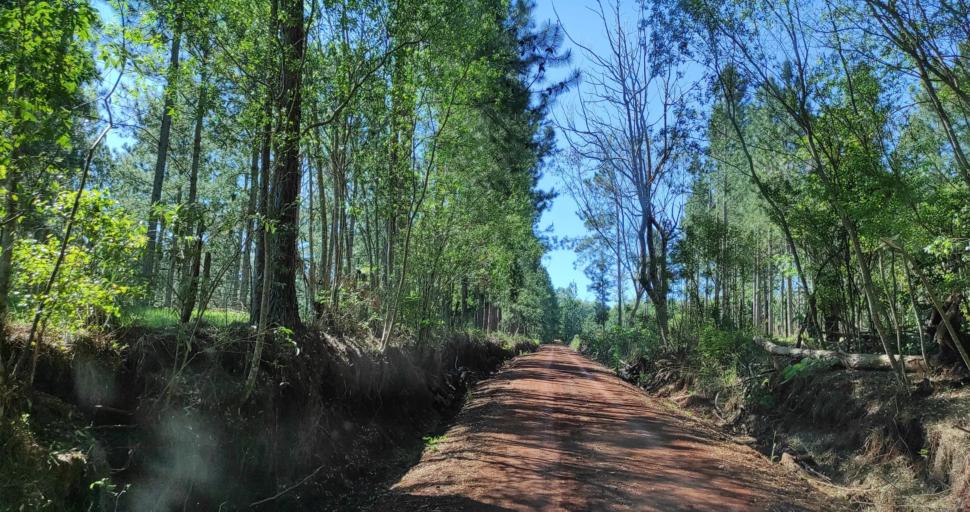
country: AR
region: Misiones
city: Ruiz de Montoya
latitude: -26.9483
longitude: -55.0030
